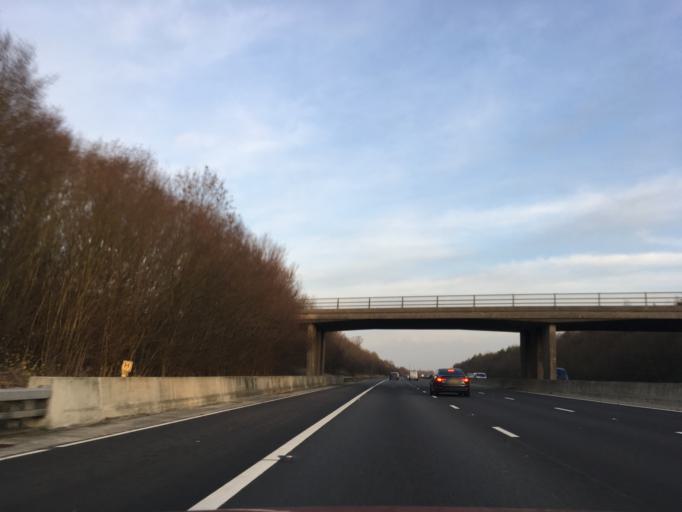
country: GB
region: England
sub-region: Gloucestershire
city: Uckington
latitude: 51.9561
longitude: -2.1278
